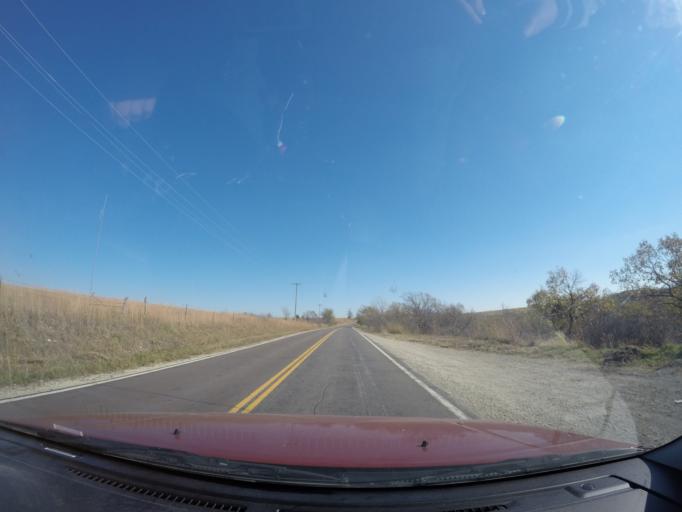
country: US
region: Kansas
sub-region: Geary County
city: Grandview Plaza
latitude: 39.0267
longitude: -96.7736
